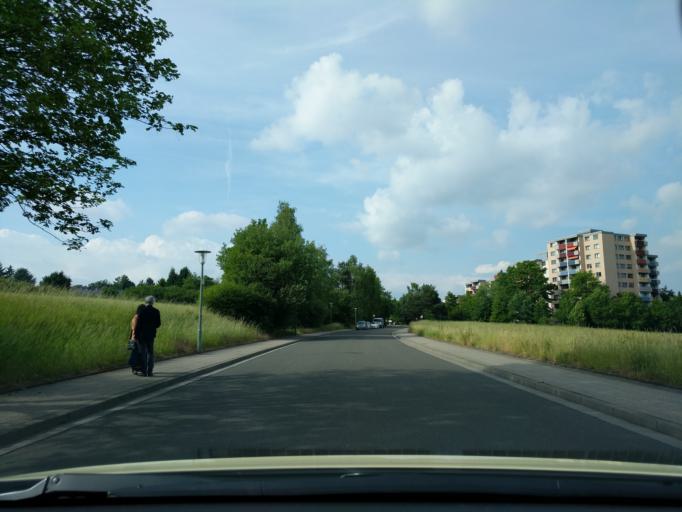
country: DE
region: Rheinland-Pfalz
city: Kaiserslautern
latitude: 49.4523
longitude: 7.7584
